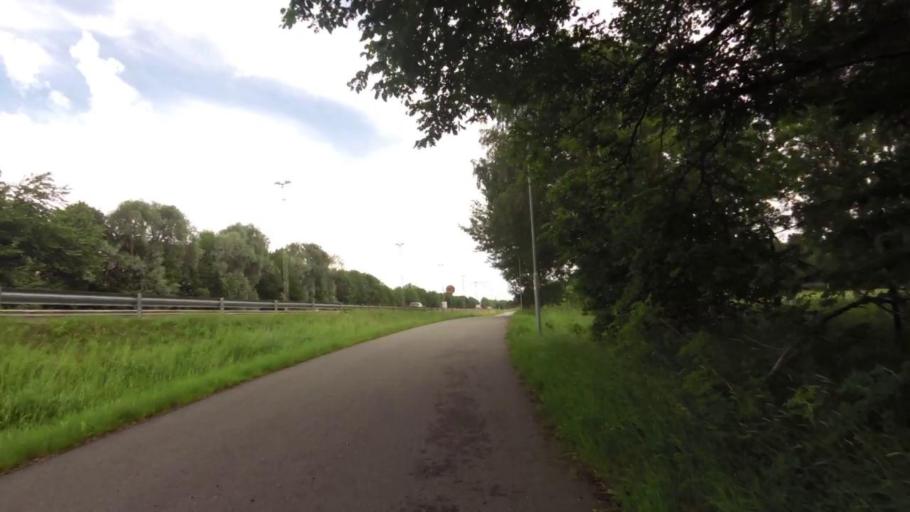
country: SE
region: OEstergoetland
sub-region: Linkopings Kommun
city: Malmslatt
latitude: 58.4045
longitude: 15.5683
